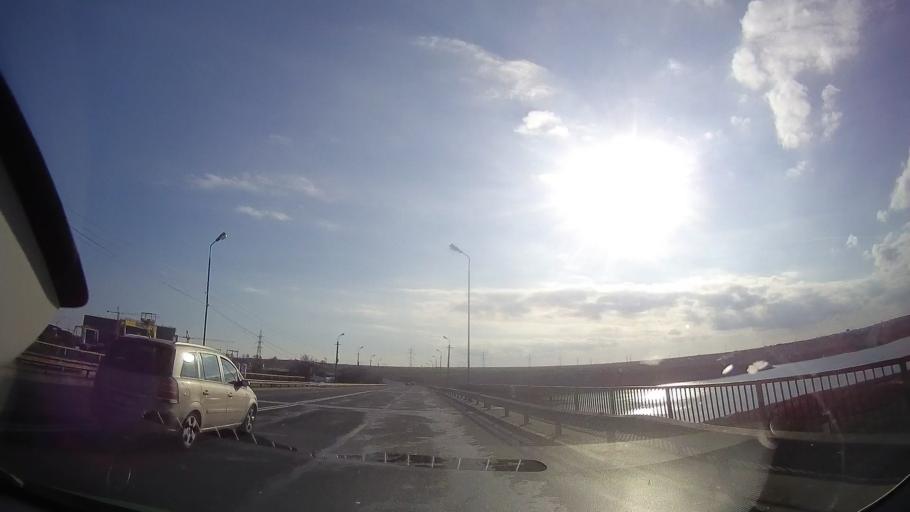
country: RO
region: Constanta
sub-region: Municipiul Mangalia
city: Mangalia
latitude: 43.8028
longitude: 28.5599
